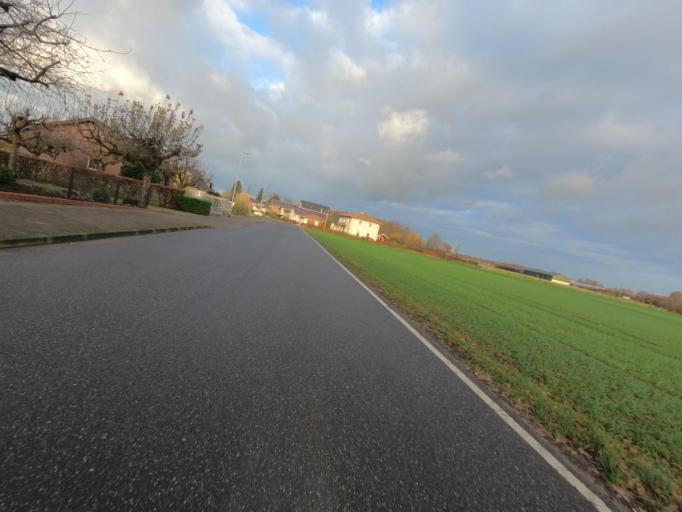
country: NL
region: Limburg
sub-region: Gemeente Roerdalen
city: Vlodrop
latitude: 51.0988
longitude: 6.0866
